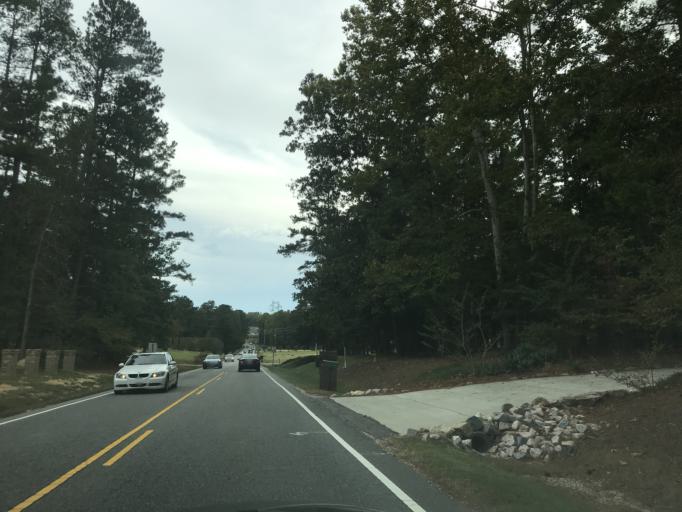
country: US
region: North Carolina
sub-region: Wake County
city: Rolesville
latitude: 35.9196
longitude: -78.5054
